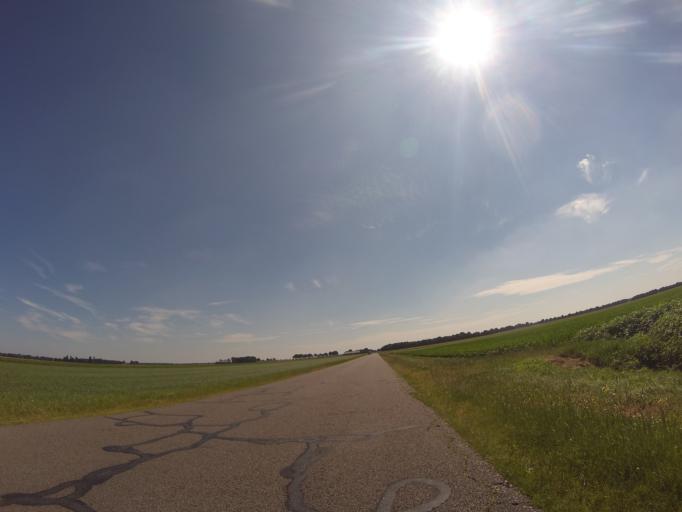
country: NL
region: Drenthe
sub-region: Gemeente Emmen
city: Klazienaveen
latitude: 52.6893
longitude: 6.9624
